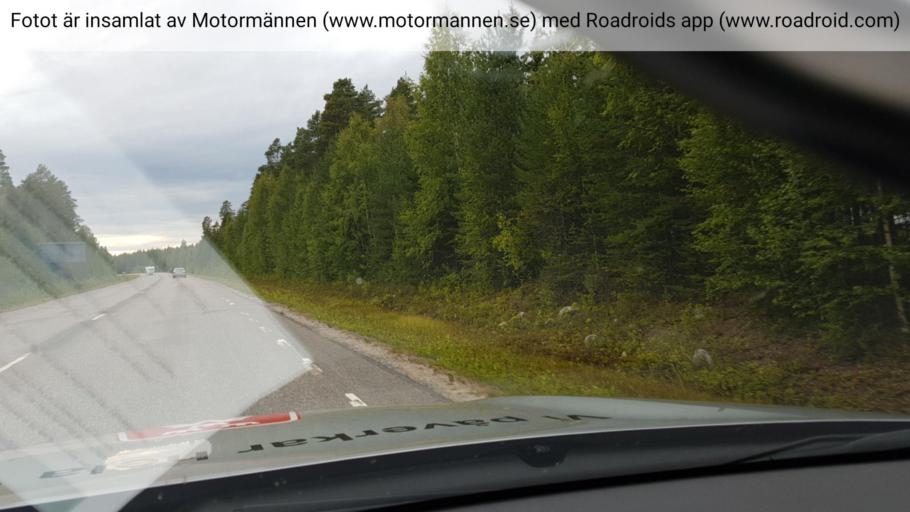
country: SE
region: Norrbotten
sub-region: Lulea Kommun
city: Gammelstad
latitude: 65.6629
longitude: 22.0871
